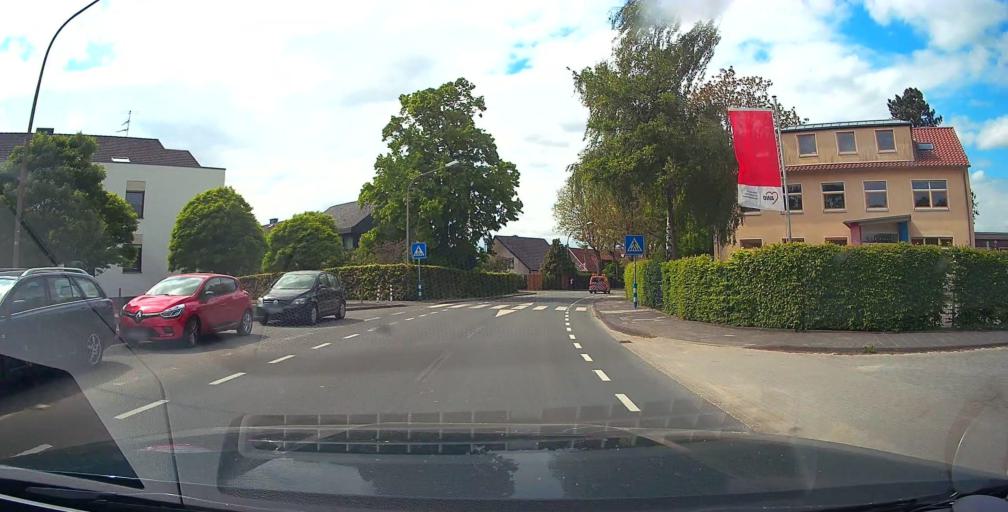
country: DE
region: North Rhine-Westphalia
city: Lengerich
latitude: 52.1797
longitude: 7.8438
